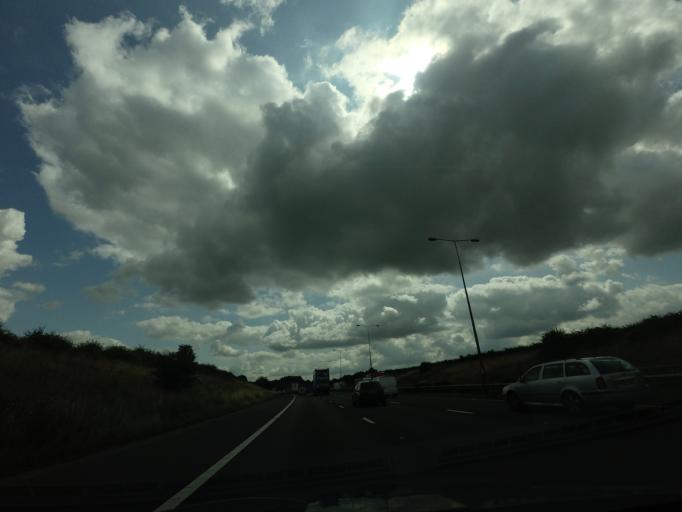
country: GB
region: England
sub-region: St. Helens
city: Billinge
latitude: 53.5154
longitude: -2.6916
